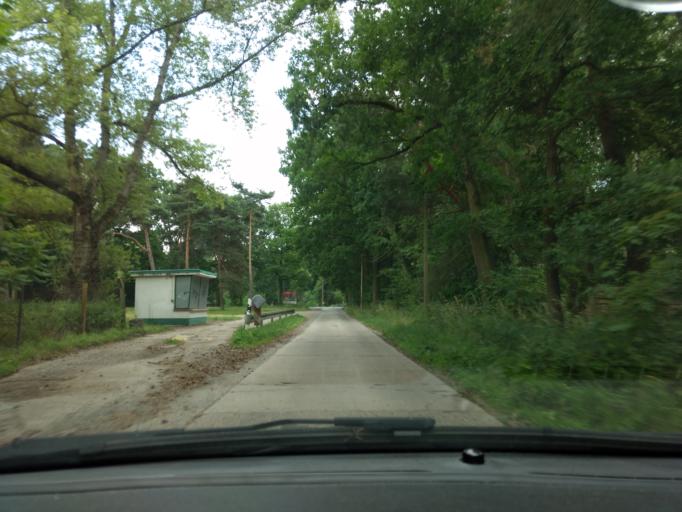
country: DE
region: Saxony
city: Radeburg
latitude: 51.2316
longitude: 13.7298
